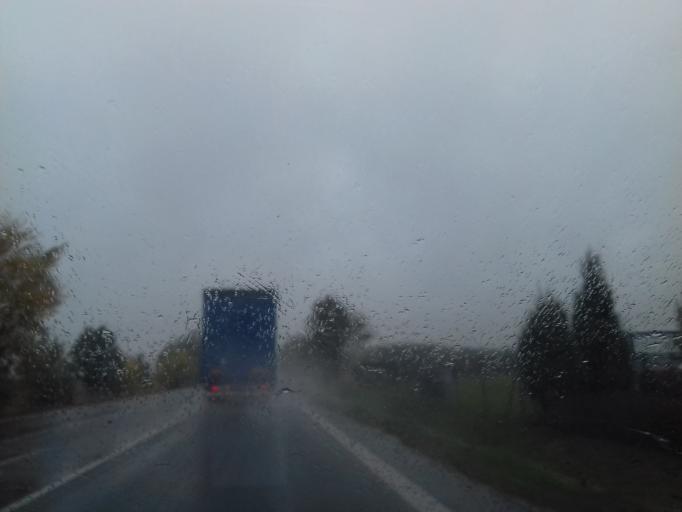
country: CZ
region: Kralovehradecky
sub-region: Okres Jicin
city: Jicin
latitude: 50.4278
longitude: 15.3762
